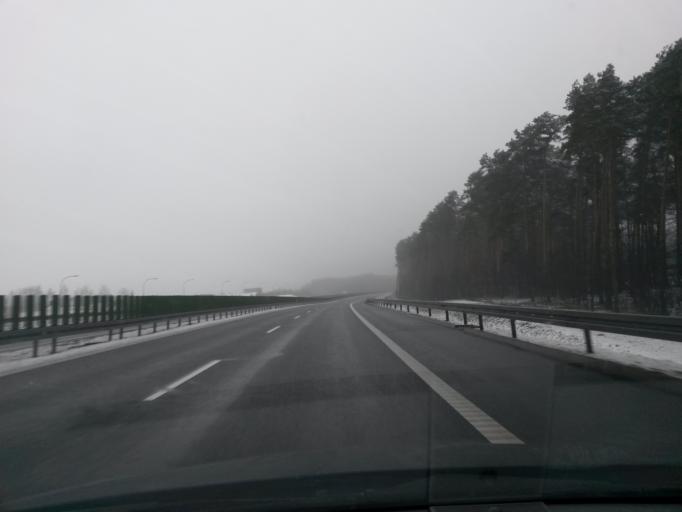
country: PL
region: Kujawsko-Pomorskie
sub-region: Powiat bydgoski
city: Biale Blota
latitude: 53.0736
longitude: 17.9189
